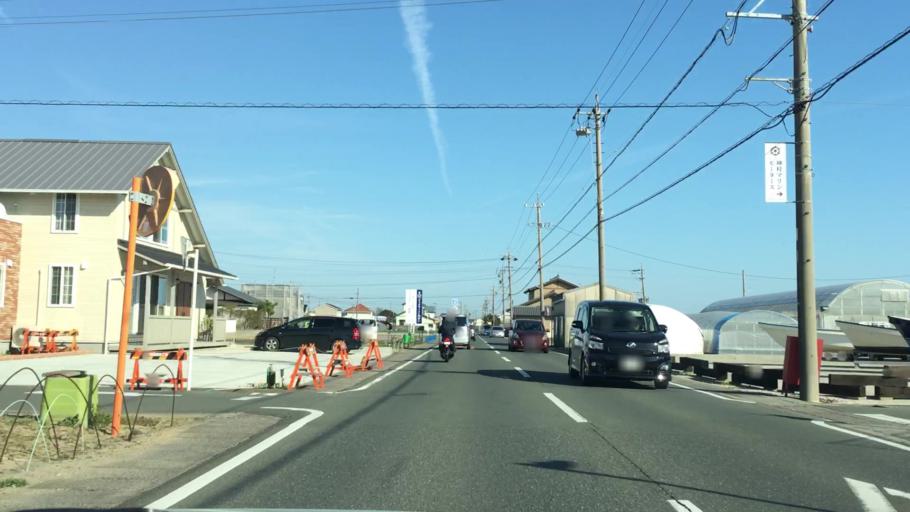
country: JP
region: Shizuoka
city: Kosai-shi
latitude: 34.7001
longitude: 137.6192
